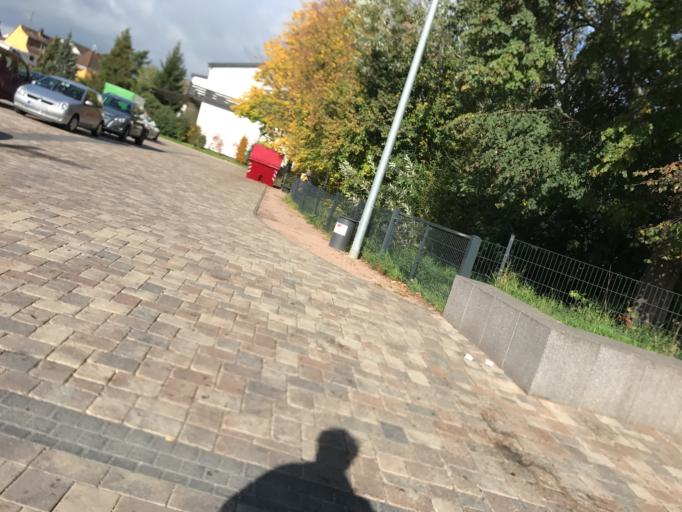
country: DE
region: Rheinland-Pfalz
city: Gau-Algesheim
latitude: 49.9580
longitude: 8.0178
